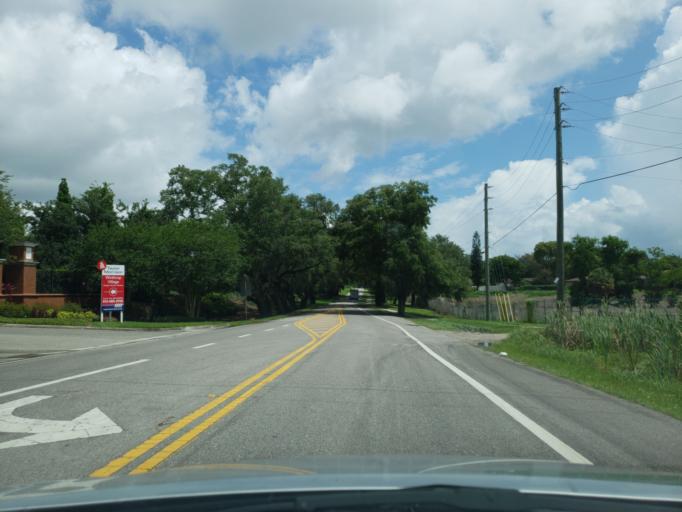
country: US
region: Florida
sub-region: Hillsborough County
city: Riverview
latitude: 27.8898
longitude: -82.3103
